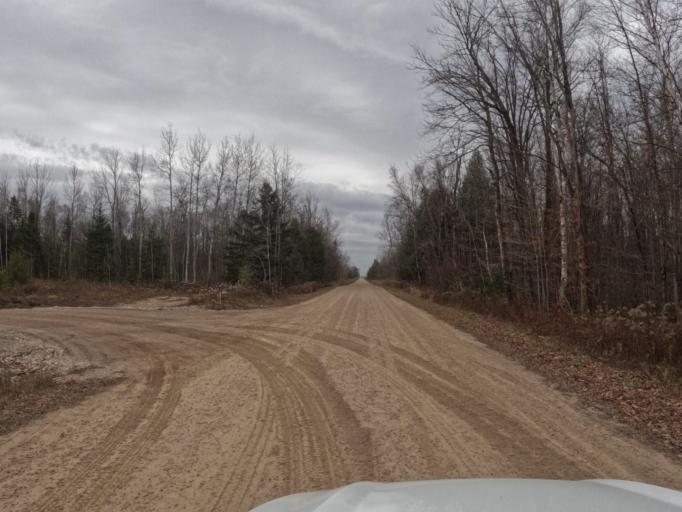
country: CA
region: Ontario
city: Shelburne
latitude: 44.0303
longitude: -80.3941
